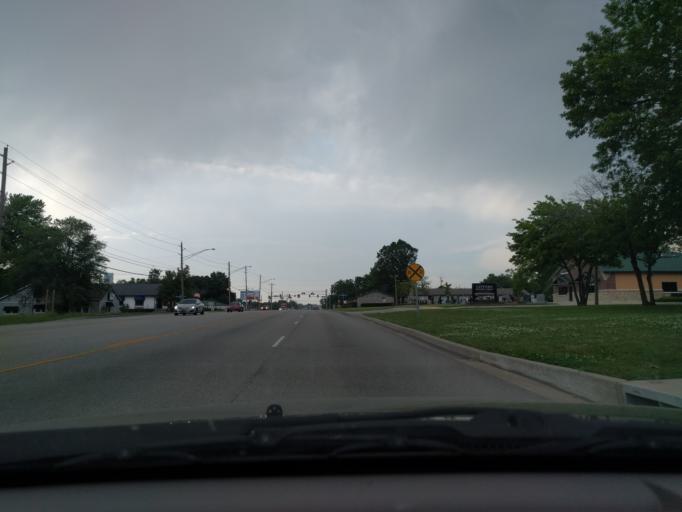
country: US
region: Oklahoma
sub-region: Tulsa County
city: Broken Arrow
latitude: 36.0504
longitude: -95.7974
